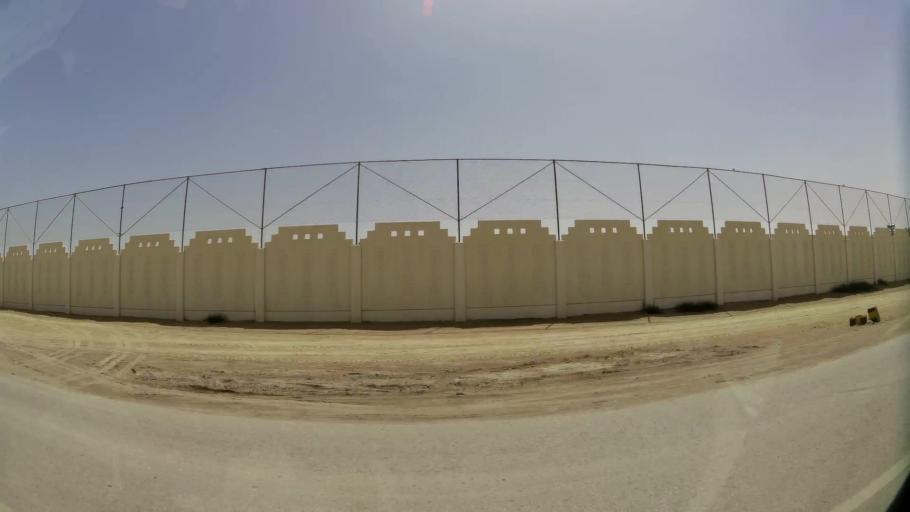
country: QA
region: Baladiyat Umm Salal
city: Umm Salal Muhammad
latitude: 25.3973
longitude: 51.4457
